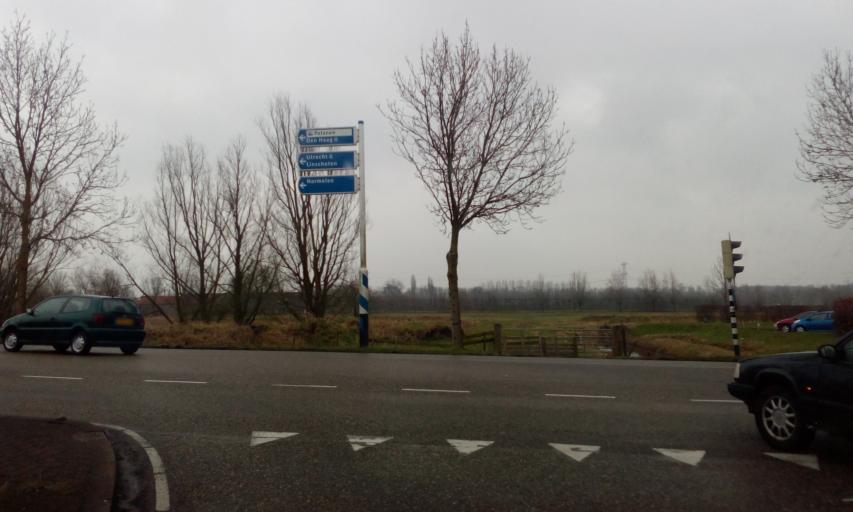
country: NL
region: Utrecht
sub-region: Gemeente Woerden
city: Woerden
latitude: 52.0758
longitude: 4.8968
